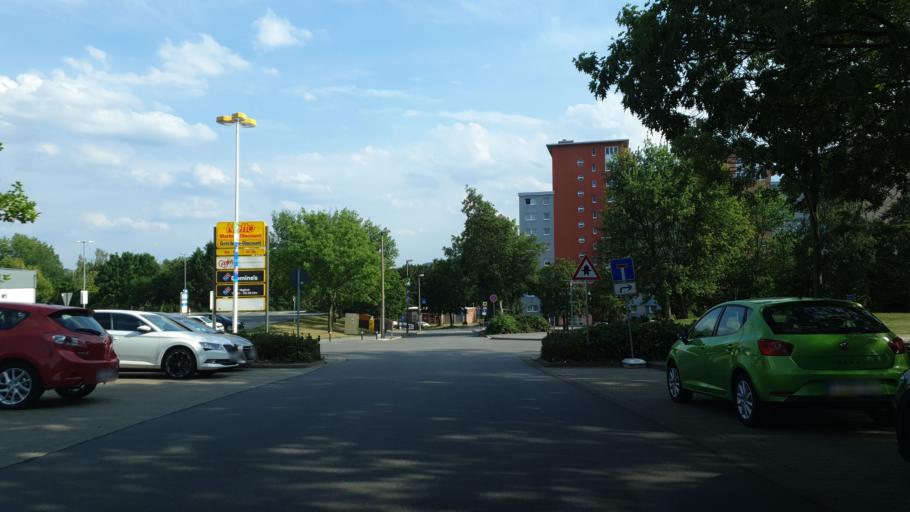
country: DE
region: Saxony
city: Neukirchen
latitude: 50.7933
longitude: 12.8843
